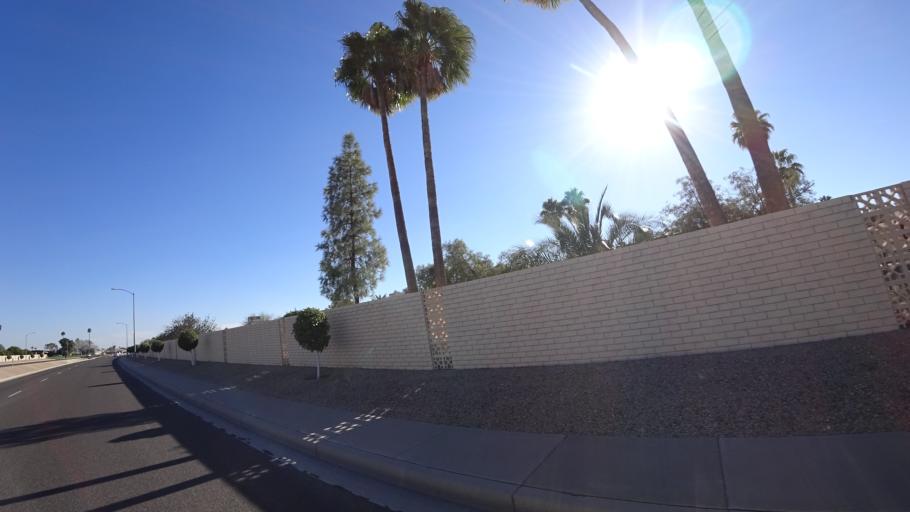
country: US
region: Arizona
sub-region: Maricopa County
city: Sun City West
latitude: 33.6729
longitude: -112.3351
